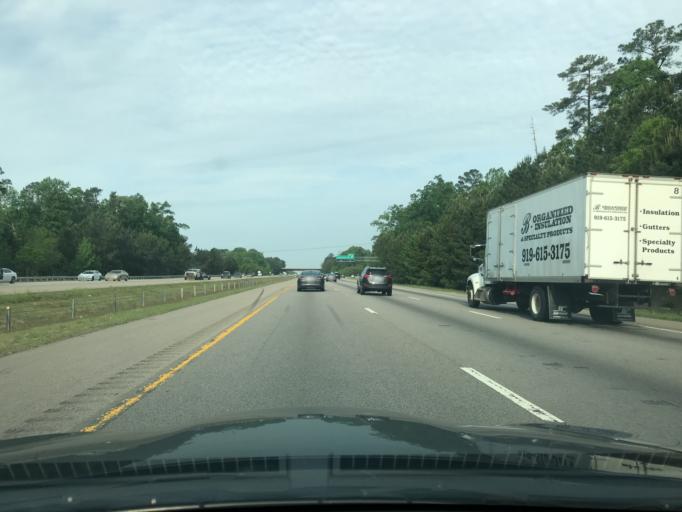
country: US
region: North Carolina
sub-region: Wake County
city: Cary
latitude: 35.9127
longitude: -78.7203
